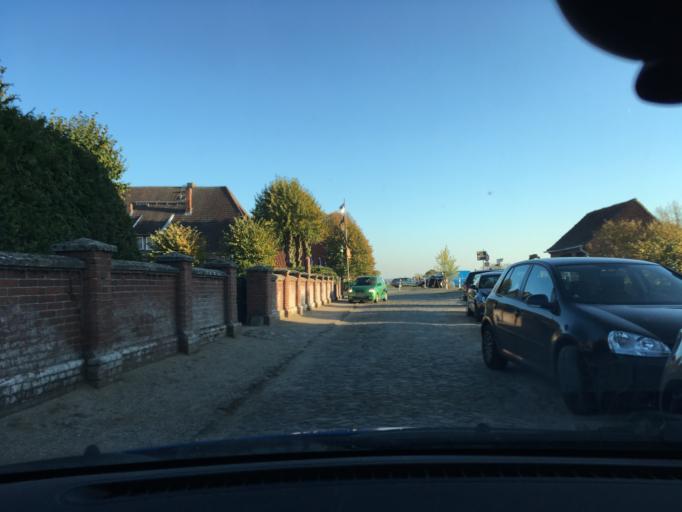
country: DE
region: Lower Saxony
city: Bleckede
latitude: 53.2886
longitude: 10.8012
